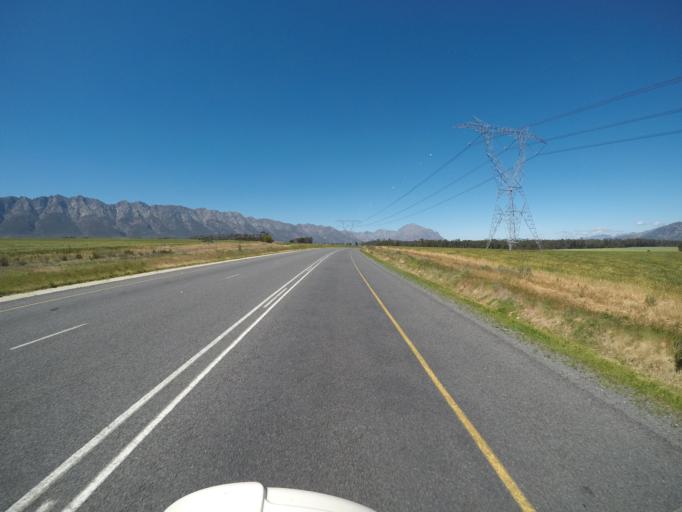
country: ZA
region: Western Cape
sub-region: Cape Winelands District Municipality
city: Ceres
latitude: -33.3271
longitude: 19.1534
